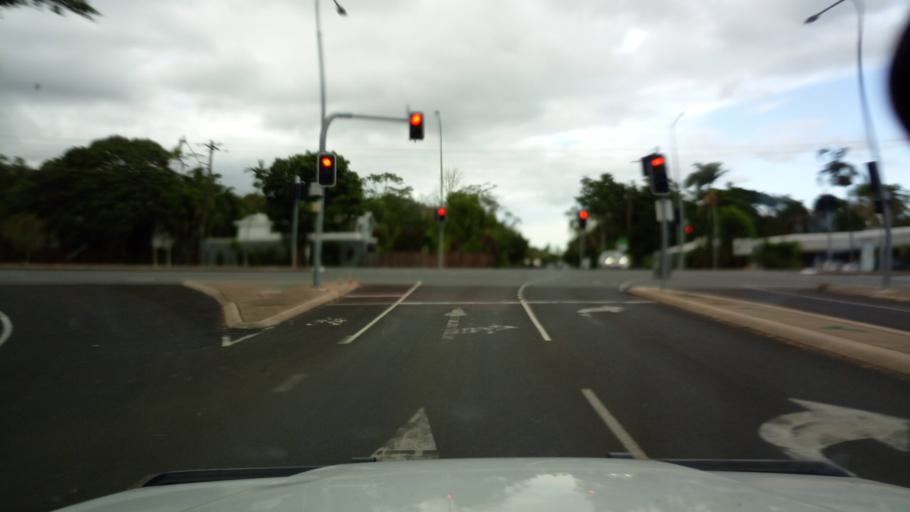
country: AU
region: Queensland
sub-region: Cairns
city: Redlynch
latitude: -16.8391
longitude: 145.6890
